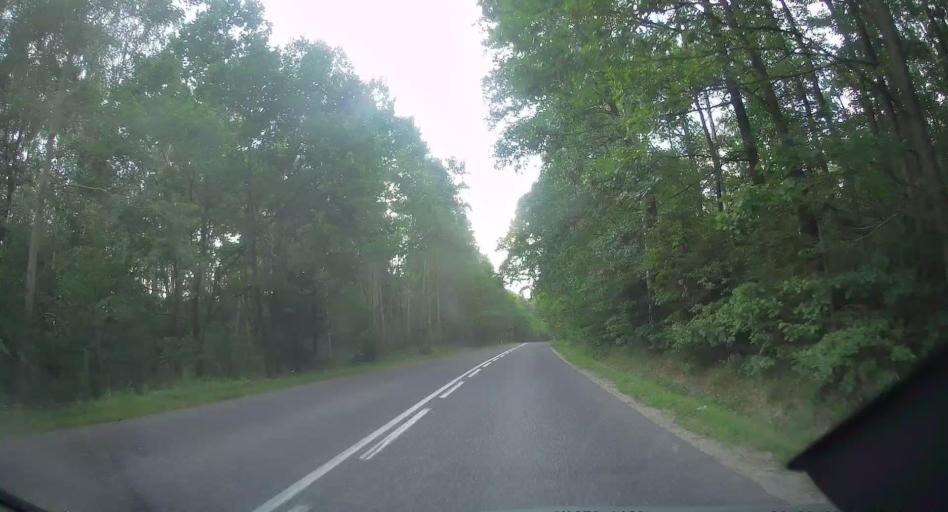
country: PL
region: Swietokrzyskie
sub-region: Powiat kielecki
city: Lopuszno
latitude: 50.8855
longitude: 20.2612
